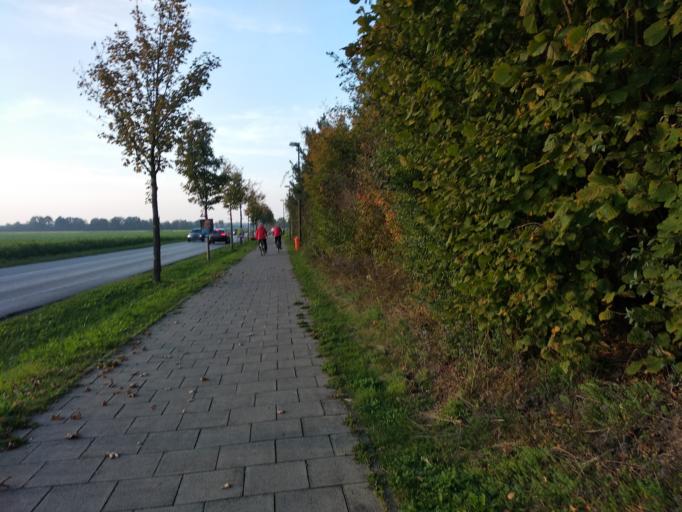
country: DE
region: Bavaria
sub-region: Upper Bavaria
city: Kirchheim bei Muenchen
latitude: 48.1658
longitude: 11.7491
